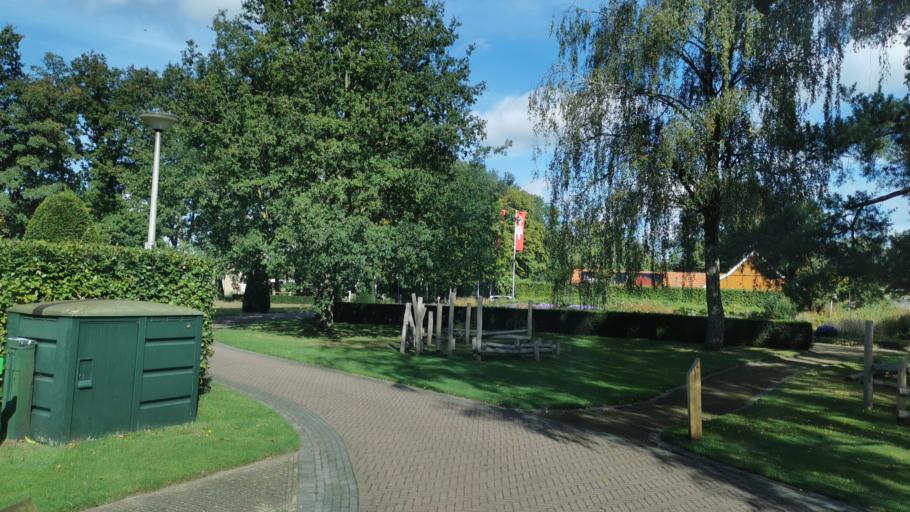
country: NL
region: Overijssel
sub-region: Gemeente Losser
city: Losser
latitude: 52.2675
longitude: 7.0134
